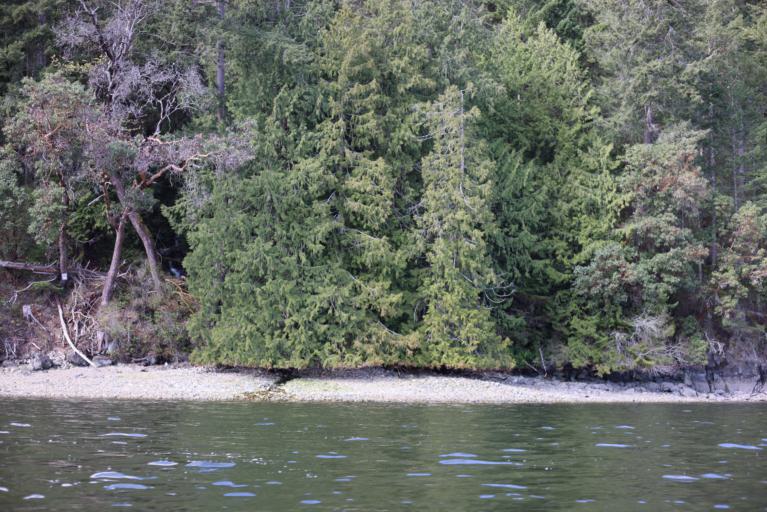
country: CA
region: British Columbia
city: Langford
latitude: 48.5461
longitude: -123.5570
